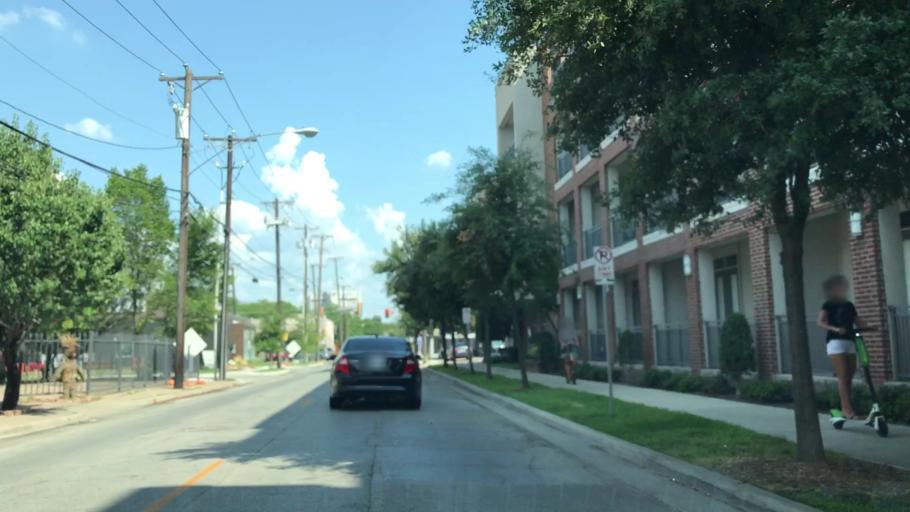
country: US
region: Texas
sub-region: Dallas County
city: Dallas
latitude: 32.7961
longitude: -96.7900
